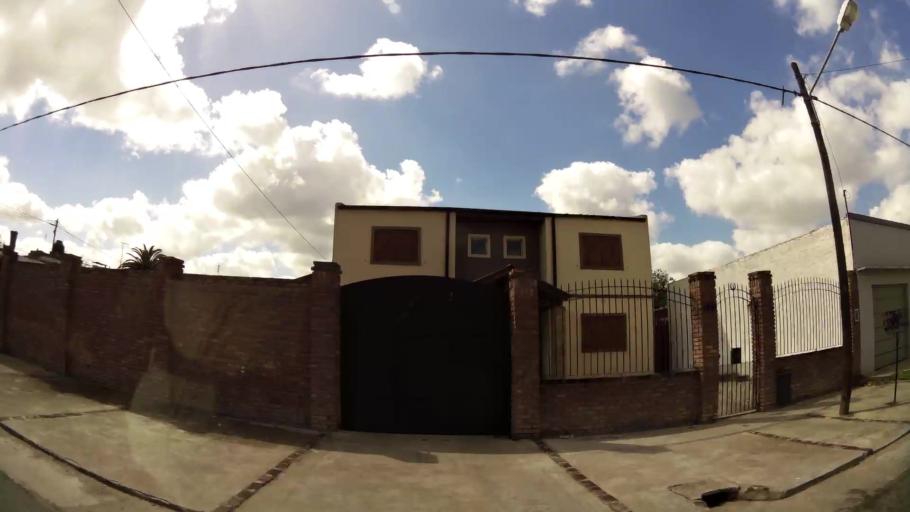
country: AR
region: Buenos Aires
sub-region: Partido de Quilmes
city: Quilmes
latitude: -34.8301
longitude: -58.1899
